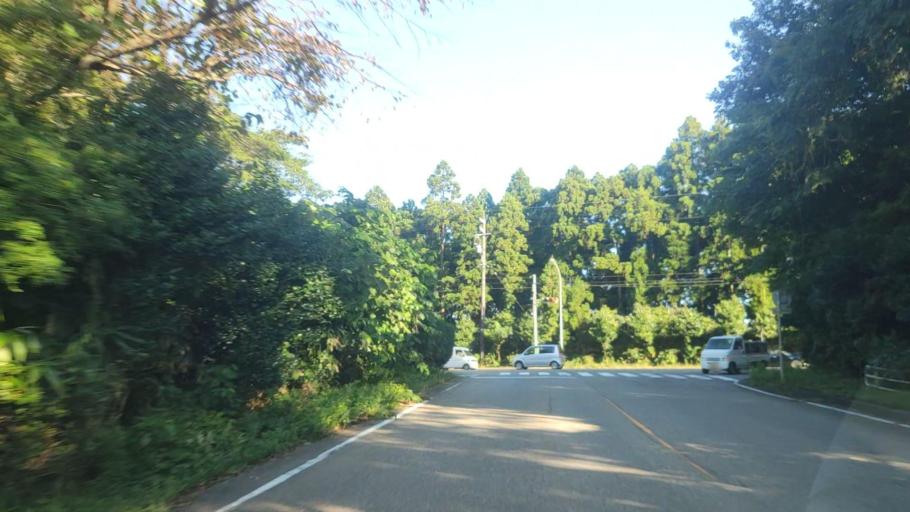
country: JP
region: Ishikawa
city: Nanao
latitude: 37.0988
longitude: 136.9510
